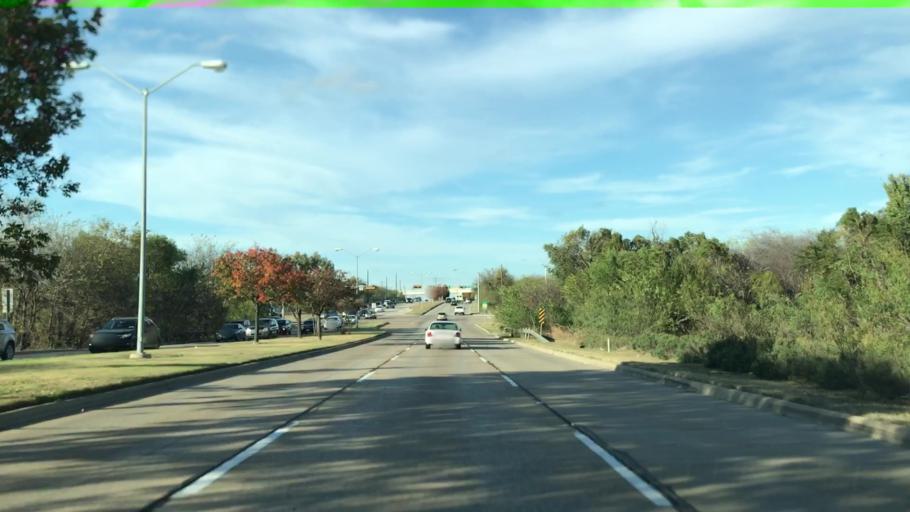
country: US
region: Texas
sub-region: Dallas County
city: Coppell
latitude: 32.8874
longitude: -96.9911
